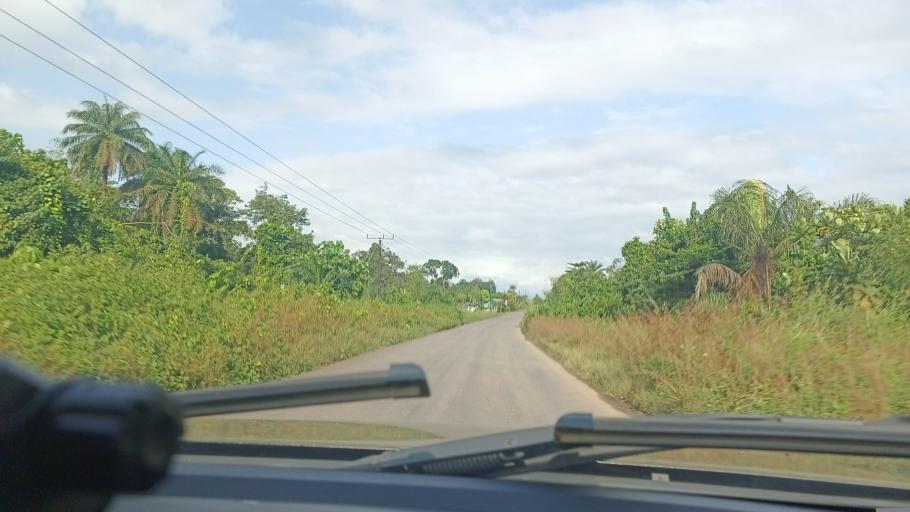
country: LR
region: Bomi
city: Tubmanburg
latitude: 6.6975
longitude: -10.9082
